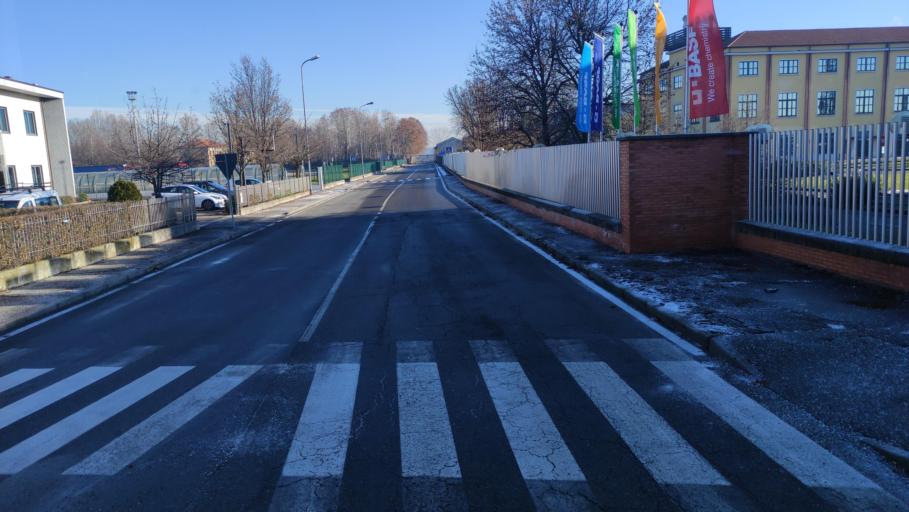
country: IT
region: Lombardy
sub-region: Provincia di Monza e Brianza
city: Villaggio del Sole
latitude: 45.6312
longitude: 9.1109
